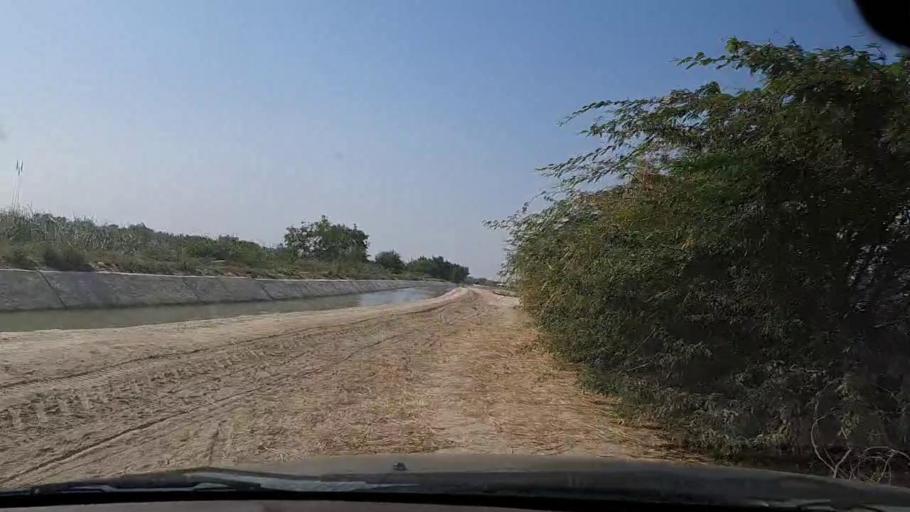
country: PK
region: Sindh
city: Chuhar Jamali
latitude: 24.4280
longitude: 67.8051
